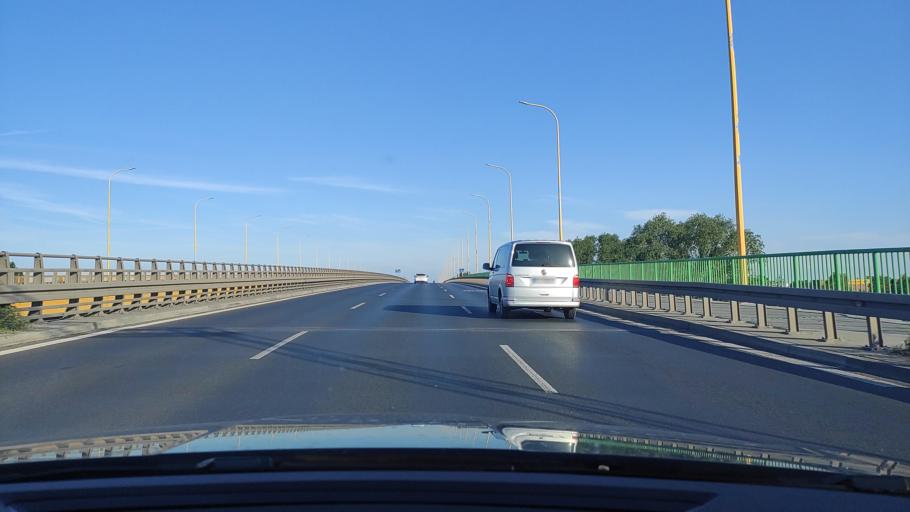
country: PL
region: Greater Poland Voivodeship
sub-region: Poznan
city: Poznan
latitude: 52.3746
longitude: 16.9838
